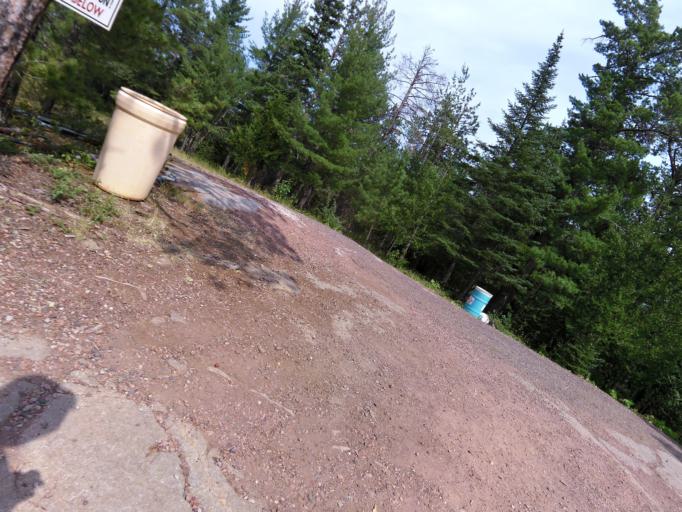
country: CA
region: Ontario
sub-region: Thunder Bay District
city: Thunder Bay
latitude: 48.8020
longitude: -88.6165
